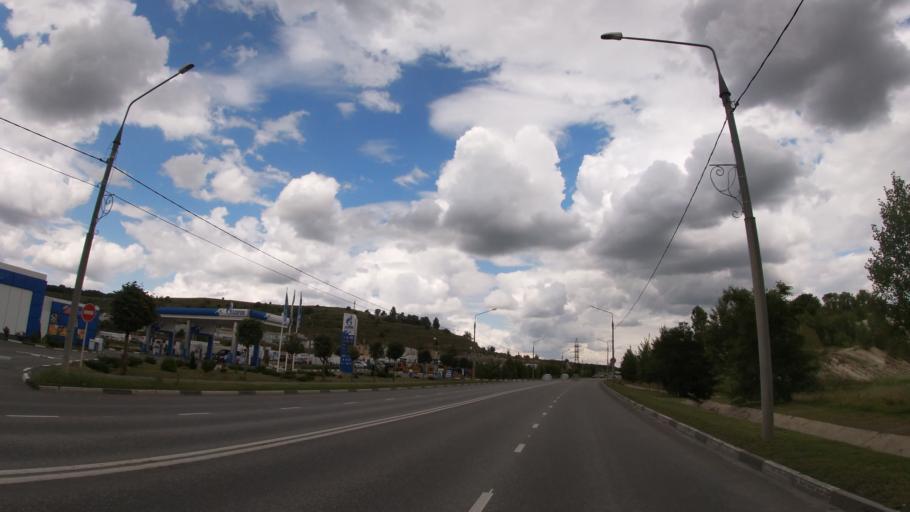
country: RU
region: Belgorod
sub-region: Belgorodskiy Rayon
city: Belgorod
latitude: 50.6145
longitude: 36.6136
